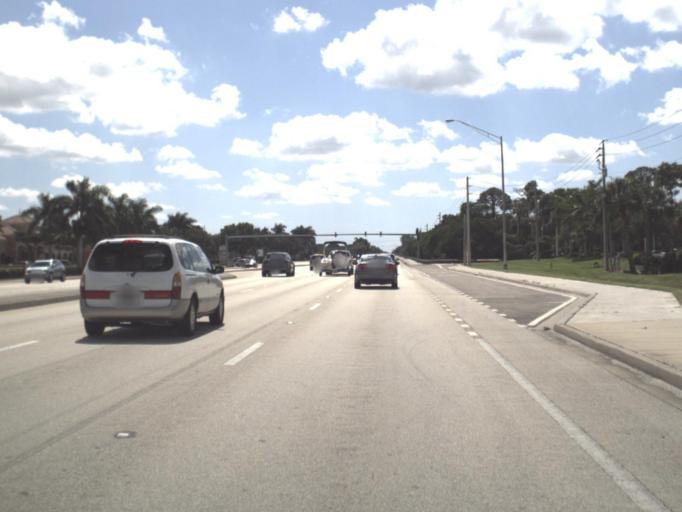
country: US
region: Florida
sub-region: Collier County
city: Naples Park
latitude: 26.2914
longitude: -81.8021
